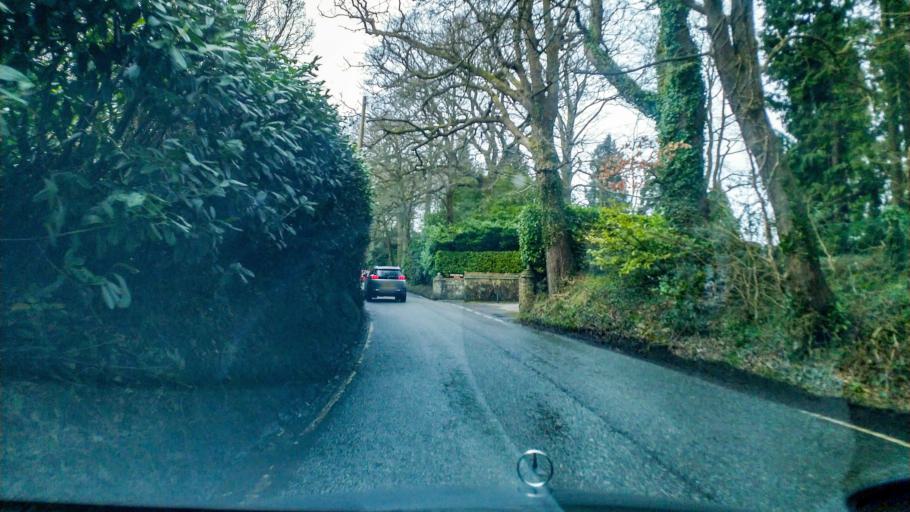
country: GB
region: England
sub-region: Surrey
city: Dorking
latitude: 51.2058
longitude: -0.3052
